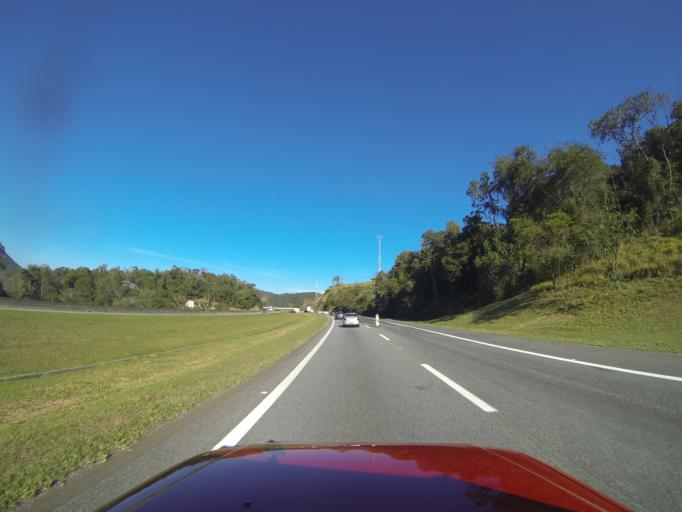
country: BR
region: Sao Paulo
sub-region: Bom Jesus Dos Perdoes
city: Bom Jesus dos Perdoes
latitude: -23.1899
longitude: -46.3576
